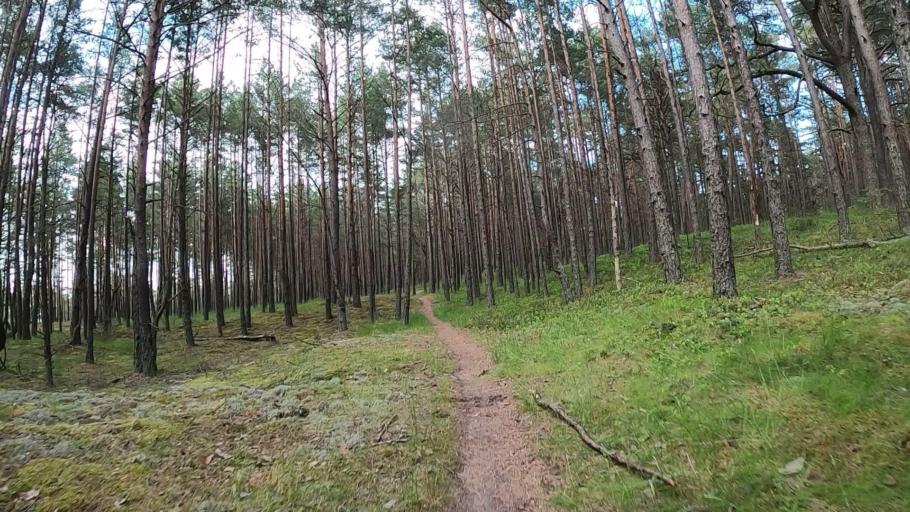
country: LV
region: Carnikava
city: Carnikava
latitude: 57.1166
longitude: 24.1985
